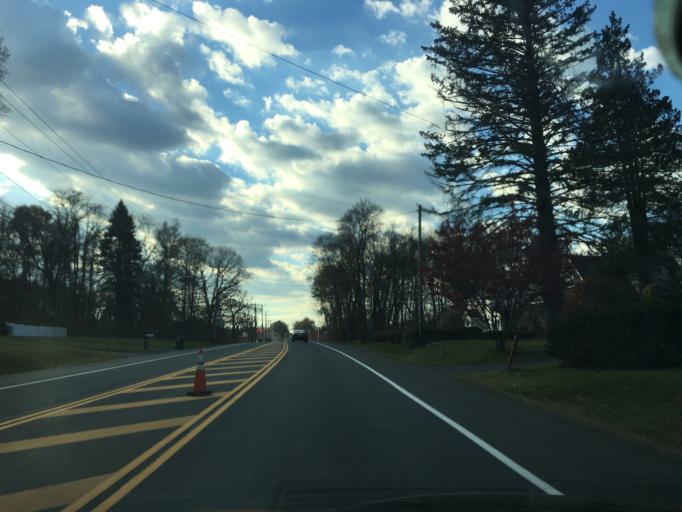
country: US
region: New York
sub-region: Albany County
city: Menands
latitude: 42.6755
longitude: -73.6910
